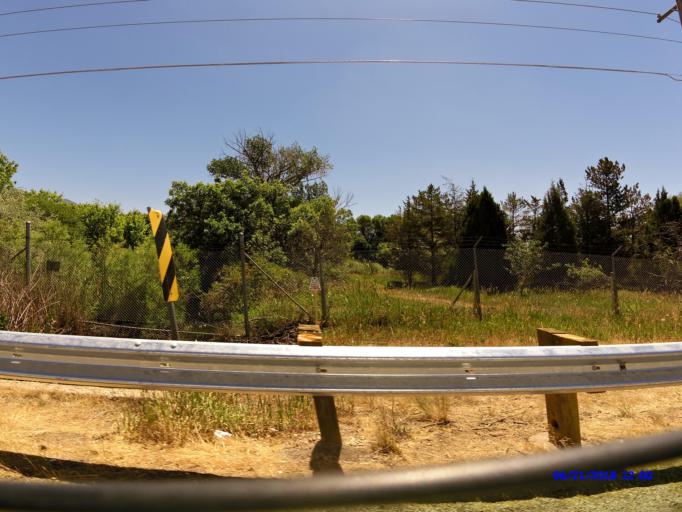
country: US
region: Utah
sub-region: Weber County
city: Marriott-Slaterville
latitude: 41.2538
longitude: -112.0094
